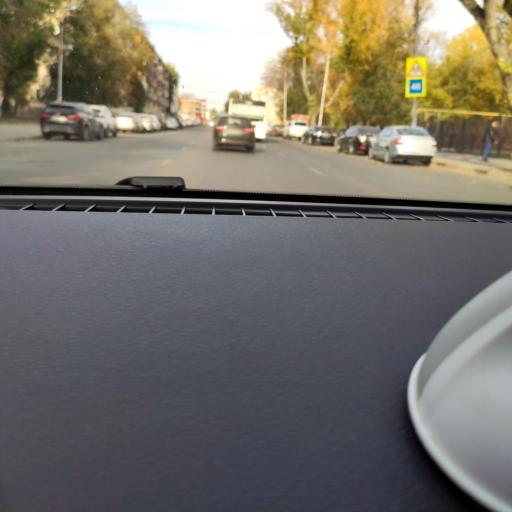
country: RU
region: Samara
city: Samara
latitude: 53.1902
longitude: 50.1234
